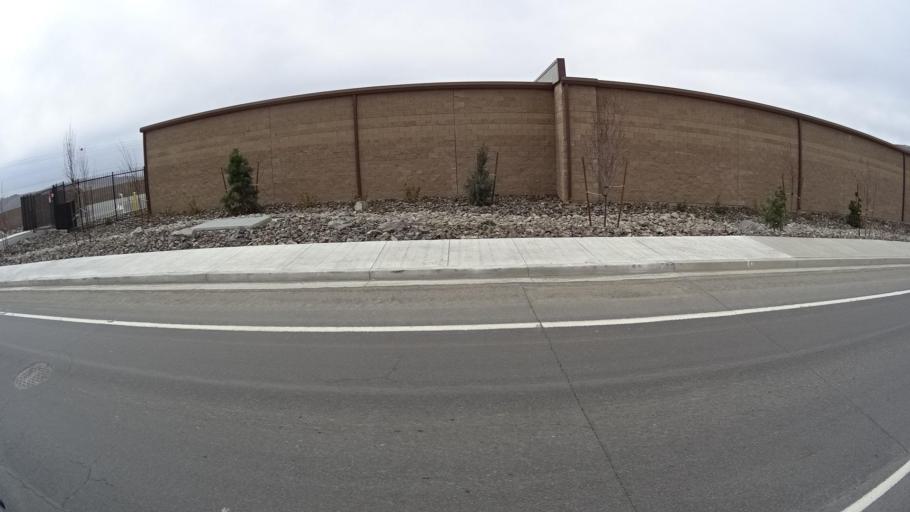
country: US
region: Nevada
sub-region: Washoe County
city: Spanish Springs
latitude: 39.6369
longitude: -119.7102
